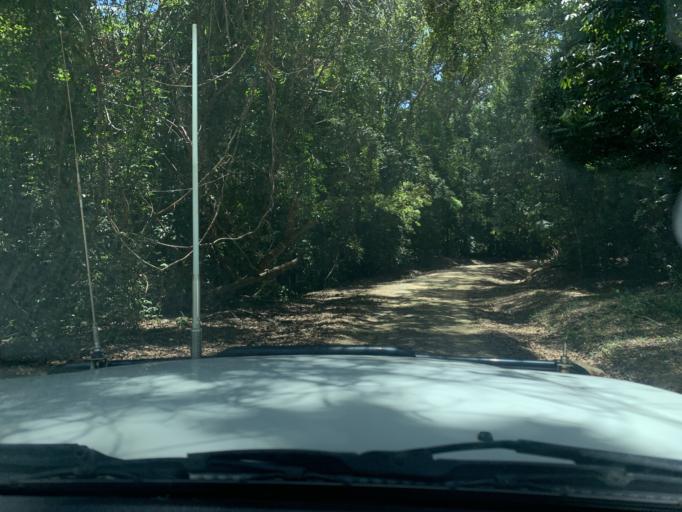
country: AU
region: Queensland
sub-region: Cairns
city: Redlynch
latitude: -16.9429
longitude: 145.6281
